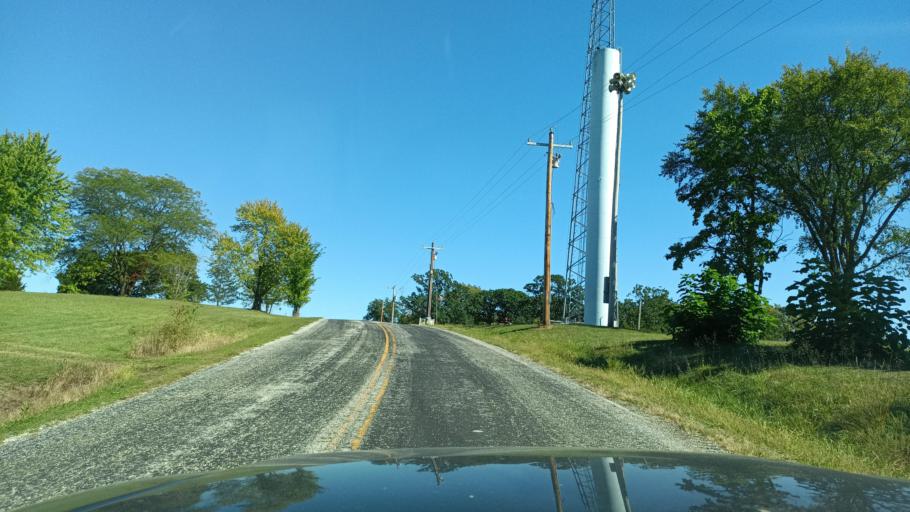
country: US
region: Missouri
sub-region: Macon County
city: La Plata
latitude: 39.9538
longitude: -92.6471
